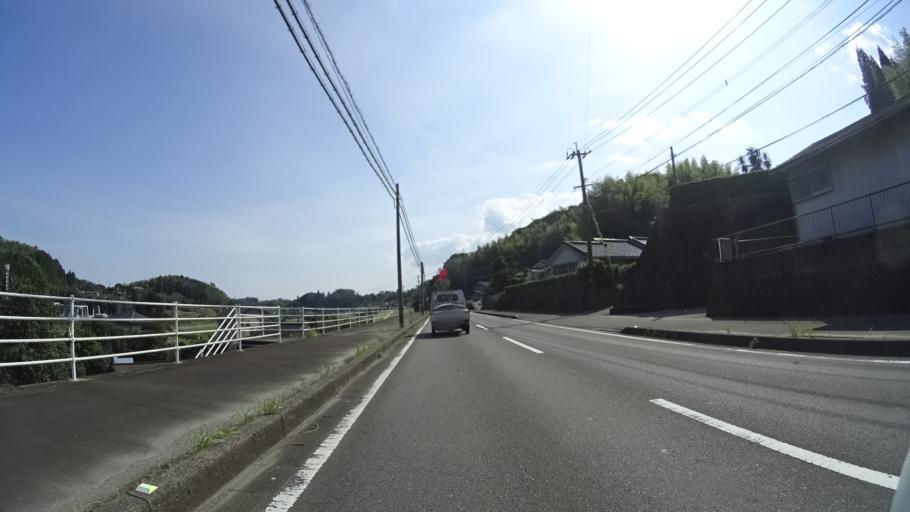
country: JP
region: Kagoshima
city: Kagoshima-shi
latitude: 31.6608
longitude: 130.5514
